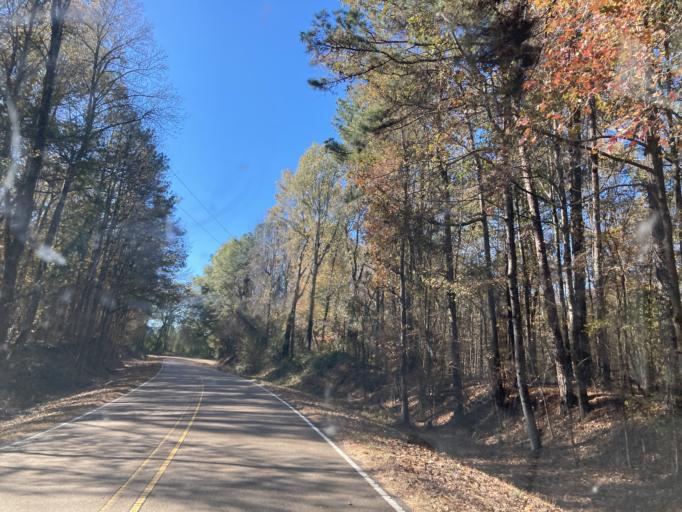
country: US
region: Mississippi
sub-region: Hinds County
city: Lynchburg
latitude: 32.5976
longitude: -90.5361
